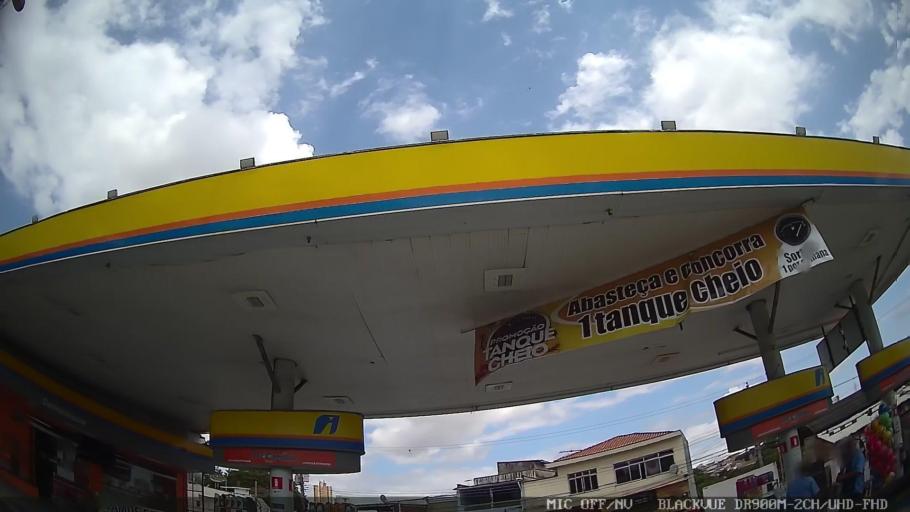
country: BR
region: Sao Paulo
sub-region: Guarulhos
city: Guarulhos
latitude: -23.5183
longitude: -46.5108
